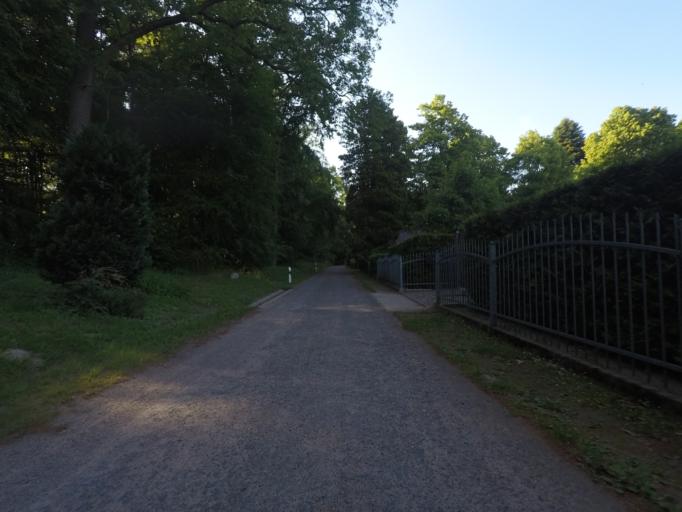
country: DE
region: Brandenburg
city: Joachimsthal
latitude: 52.9053
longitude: 13.7005
